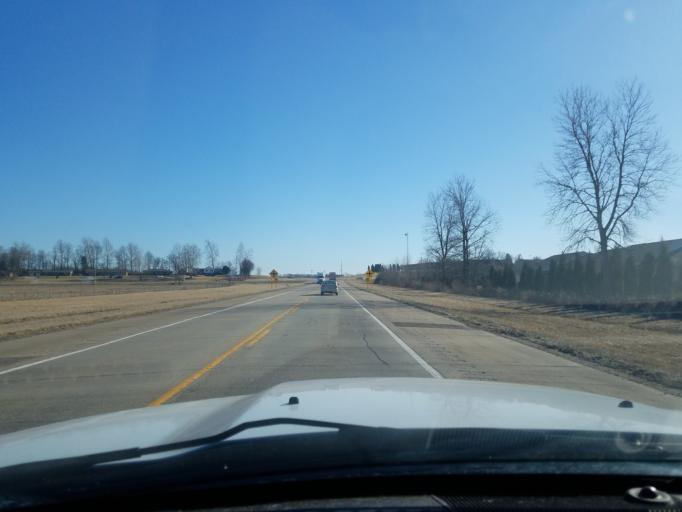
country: US
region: Kentucky
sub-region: Henderson County
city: Henderson
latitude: 37.7970
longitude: -87.6454
